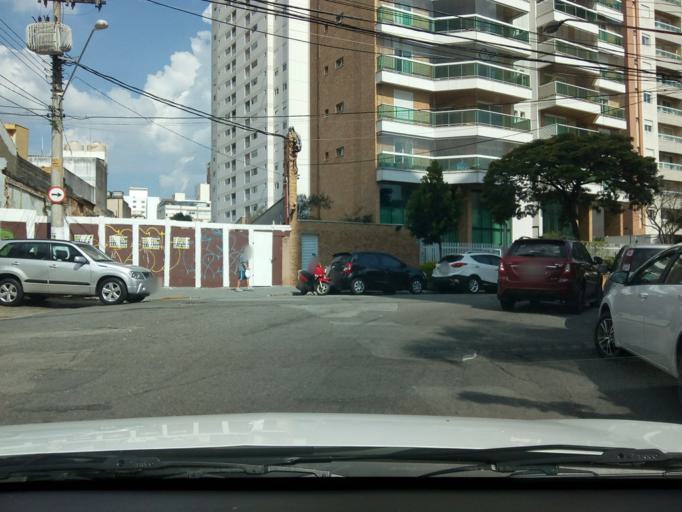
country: BR
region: Sao Paulo
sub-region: Sao Paulo
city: Sao Paulo
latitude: -23.5814
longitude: -46.6474
